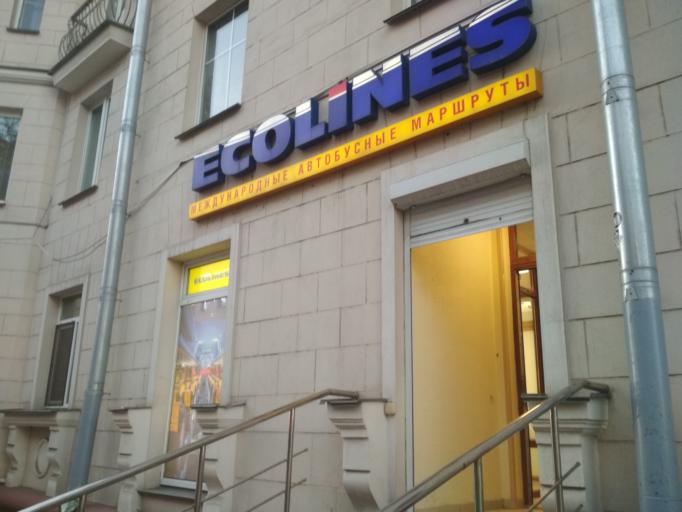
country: BY
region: Minsk
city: Minsk
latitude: 53.8903
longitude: 27.5558
